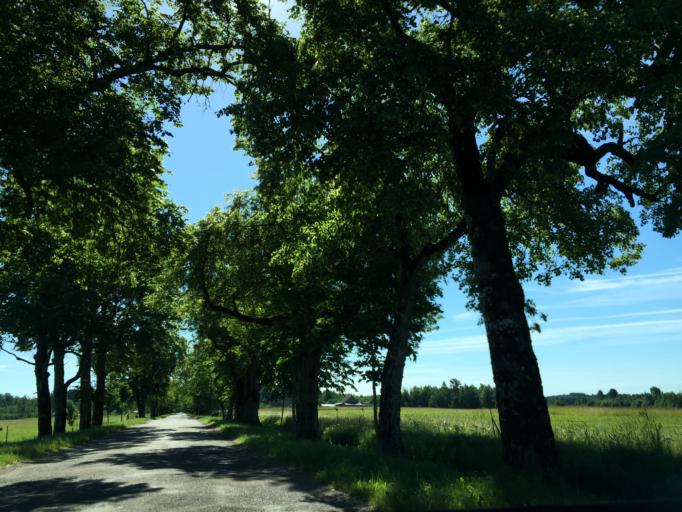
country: LV
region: Kuldigas Rajons
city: Kuldiga
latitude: 57.3259
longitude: 22.0229
